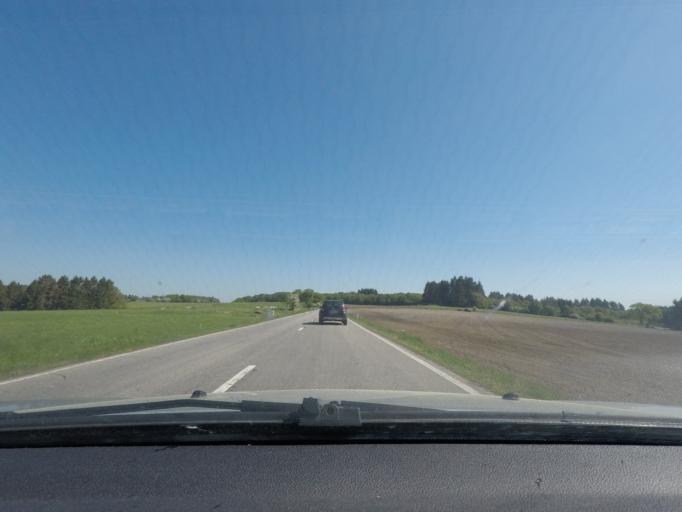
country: BE
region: Wallonia
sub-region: Province de Namur
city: Rochefort
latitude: 50.2048
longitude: 5.1422
